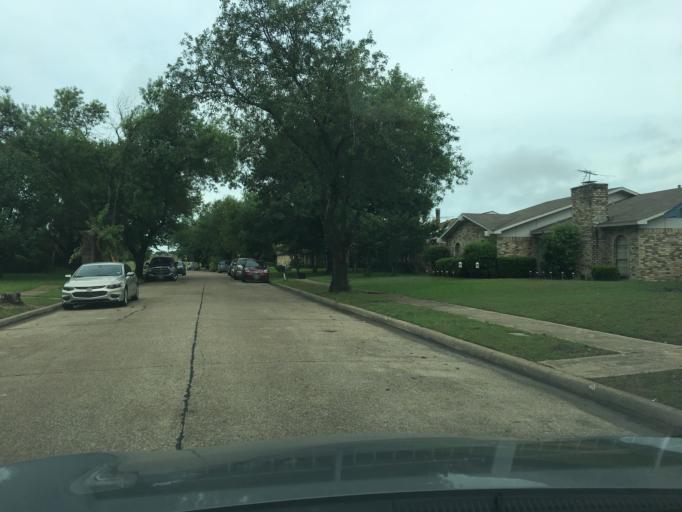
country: US
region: Texas
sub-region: Dallas County
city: Garland
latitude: 32.9569
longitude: -96.6718
